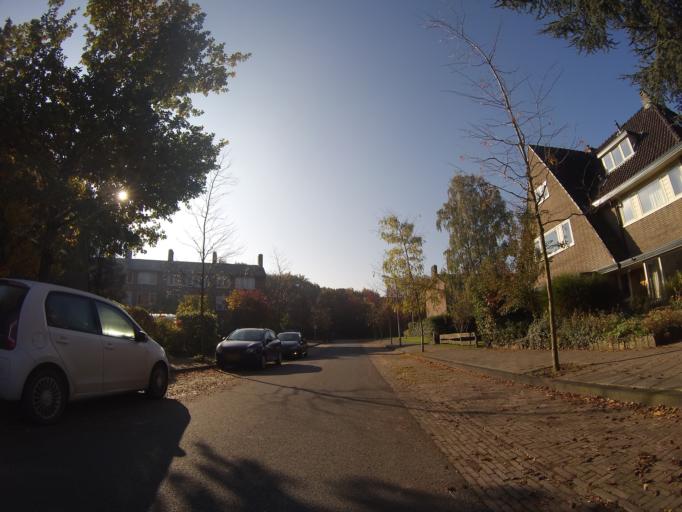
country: NL
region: Utrecht
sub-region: Gemeente Amersfoort
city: Amersfoort
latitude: 52.1407
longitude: 5.3851
